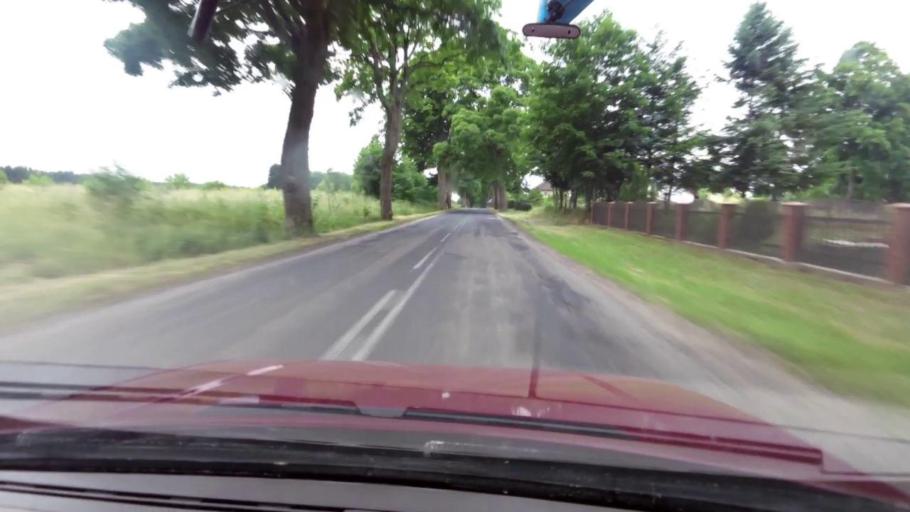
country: PL
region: West Pomeranian Voivodeship
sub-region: Powiat koszalinski
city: Sianow
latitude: 54.1743
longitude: 16.3936
